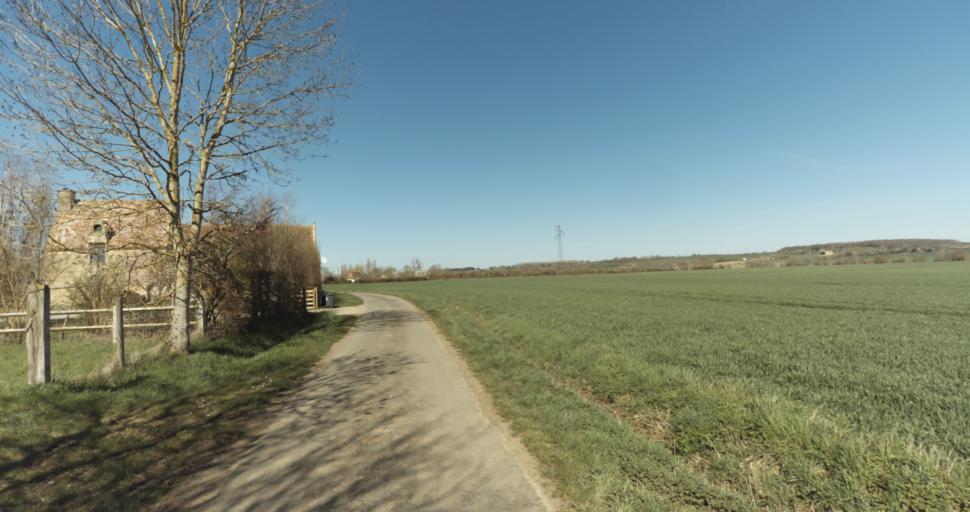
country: FR
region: Lower Normandy
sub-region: Departement du Calvados
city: Saint-Pierre-sur-Dives
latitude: 49.0277
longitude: 0.0204
